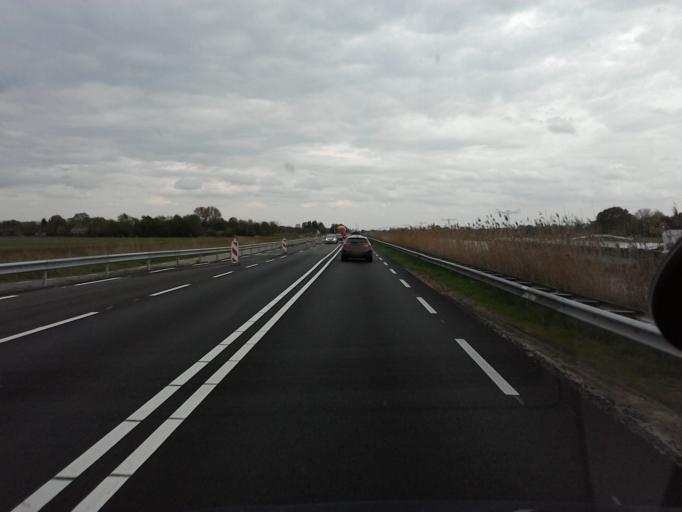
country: NL
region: North Brabant
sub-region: Gemeente Sint-Michielsgestel
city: Sint-Michielsgestel
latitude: 51.6756
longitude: 5.3818
